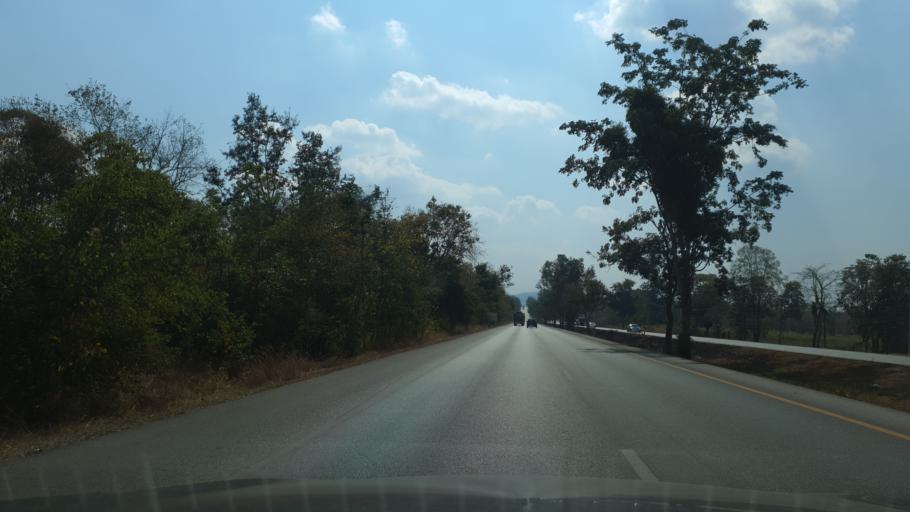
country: TH
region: Lampang
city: Mae Phrik
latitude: 17.3970
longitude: 99.1495
